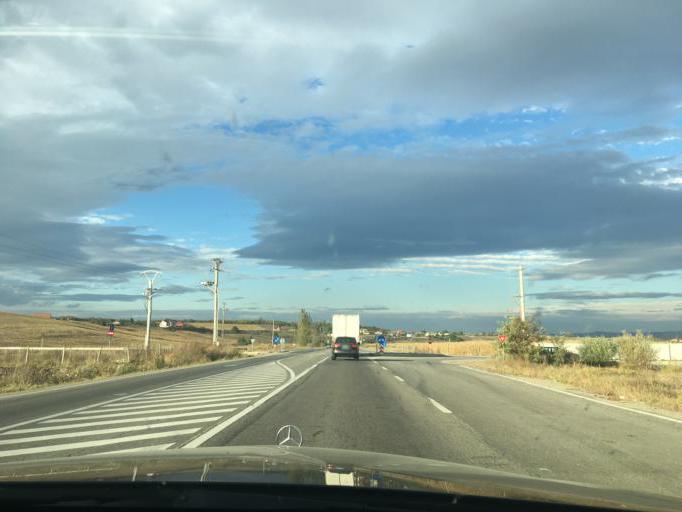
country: RO
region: Alba
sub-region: Oras Teius
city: Teius
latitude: 46.1888
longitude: 23.6619
